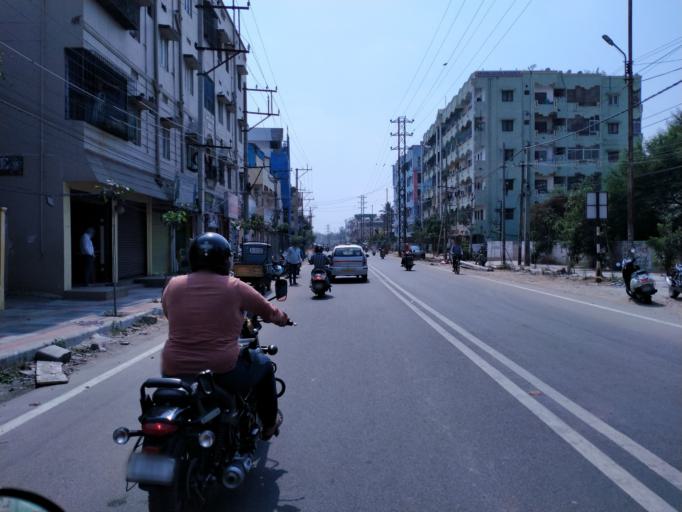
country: IN
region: Telangana
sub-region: Rangareddi
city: Secunderabad
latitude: 17.4809
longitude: 78.5368
